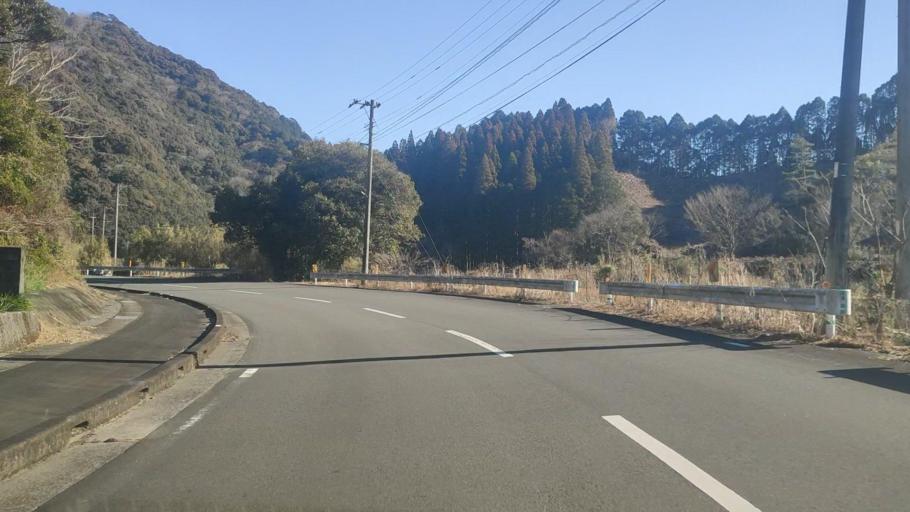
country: JP
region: Oita
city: Saiki
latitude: 32.7730
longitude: 131.8206
